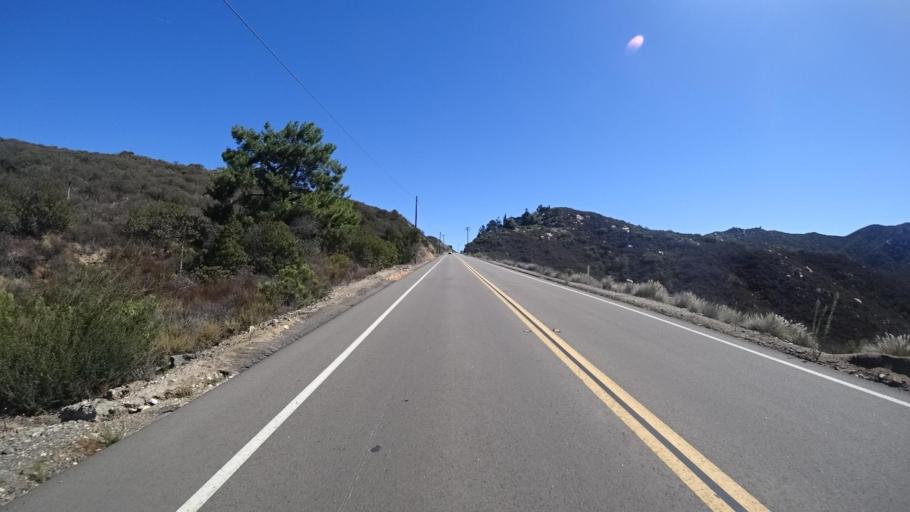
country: US
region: California
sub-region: San Diego County
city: Jamul
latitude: 32.7332
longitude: -116.8070
